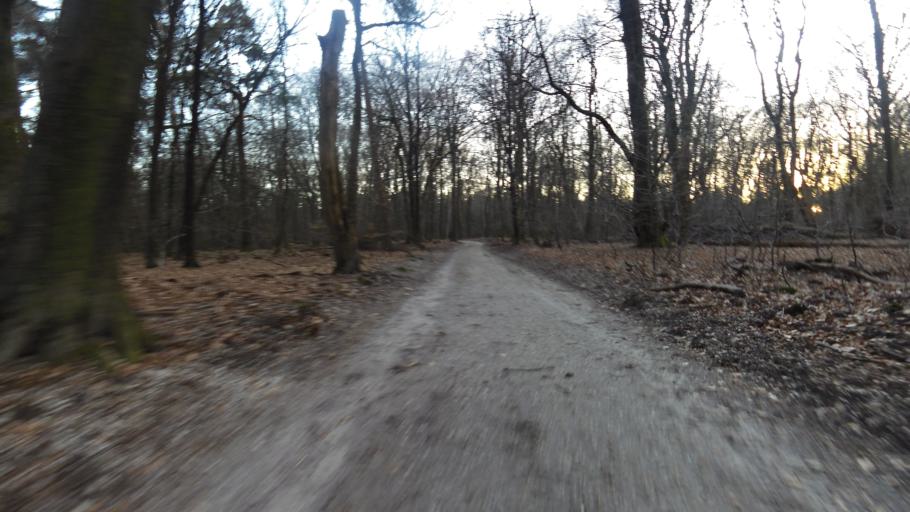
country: NL
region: Gelderland
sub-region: Gemeente Barneveld
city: Garderen
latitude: 52.2530
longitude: 5.6838
